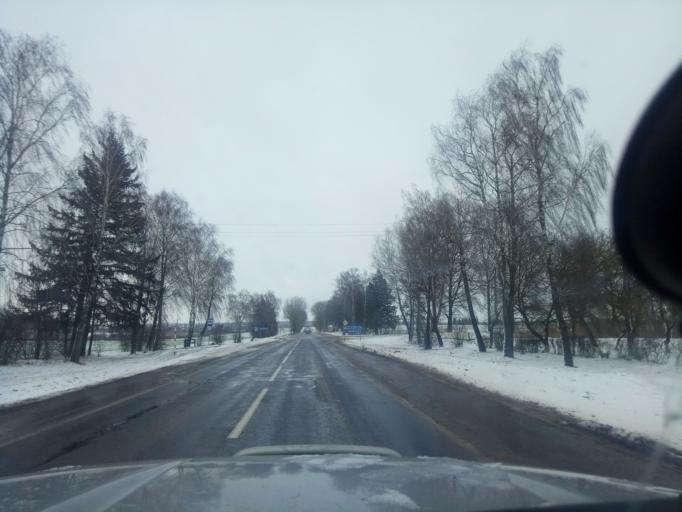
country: BY
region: Minsk
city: Tsimkavichy
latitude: 53.0899
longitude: 27.0264
